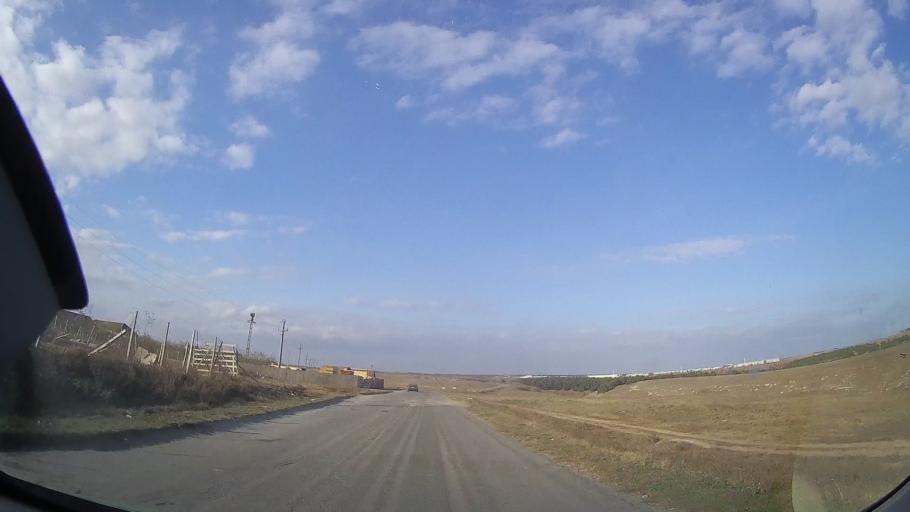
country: RO
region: Constanta
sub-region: Comuna Limanu
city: Limanu
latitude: 43.8038
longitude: 28.5212
